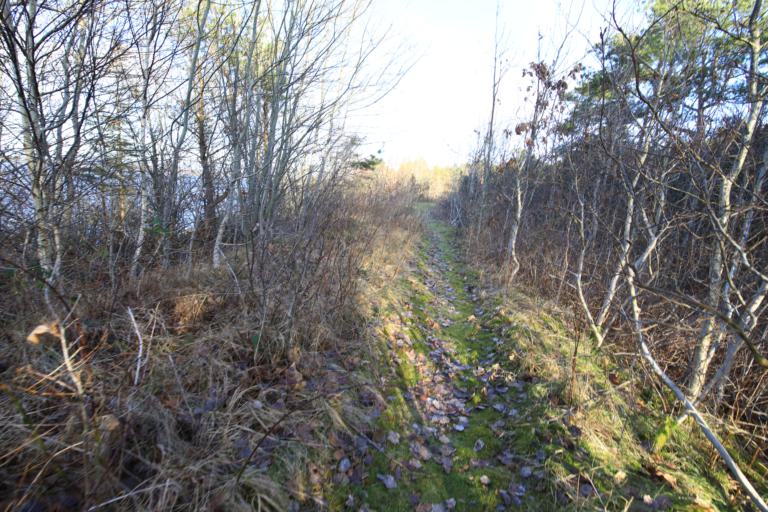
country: SE
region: Halland
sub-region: Varbergs Kommun
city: Varberg
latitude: 57.2056
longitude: 12.1974
